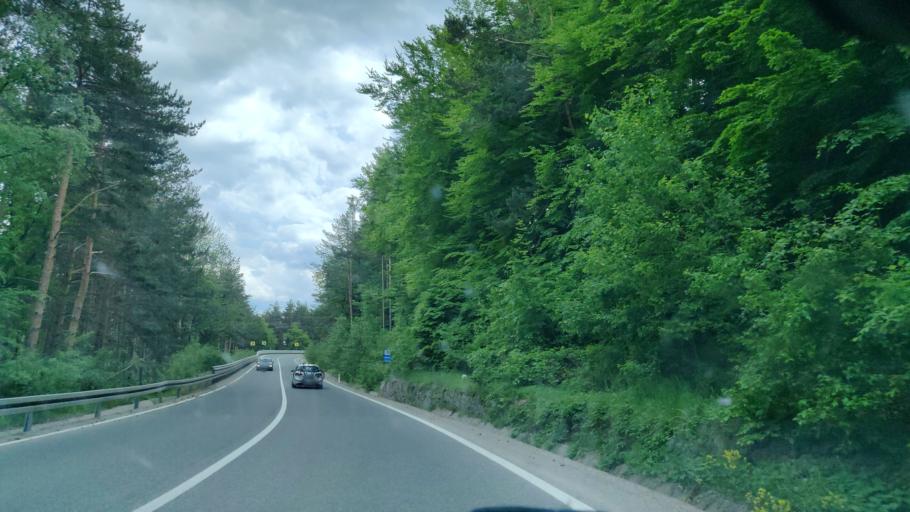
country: RO
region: Vrancea
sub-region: Comuna Tulnici
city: Tulnici
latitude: 45.9197
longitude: 26.6629
